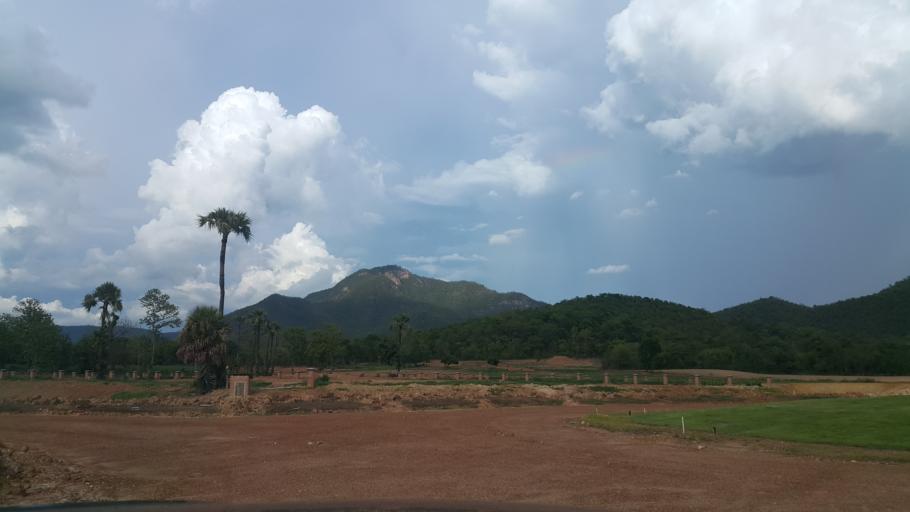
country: TH
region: Chiang Mai
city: Mae On
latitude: 18.7217
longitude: 99.2143
